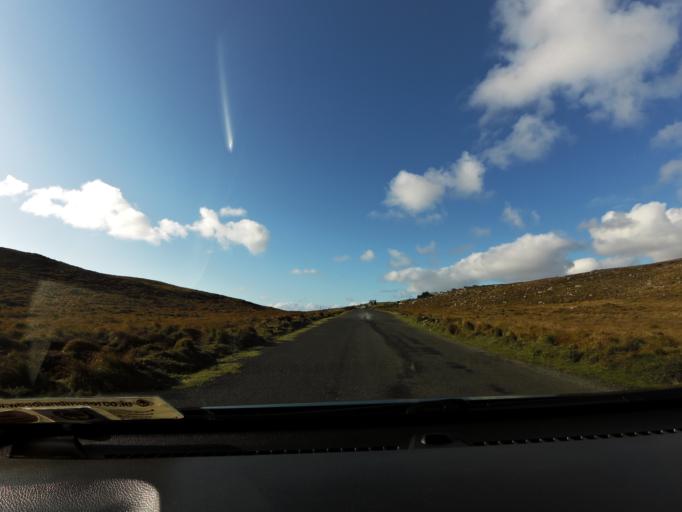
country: IE
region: Connaught
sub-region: Maigh Eo
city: Belmullet
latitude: 53.8681
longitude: -9.8865
